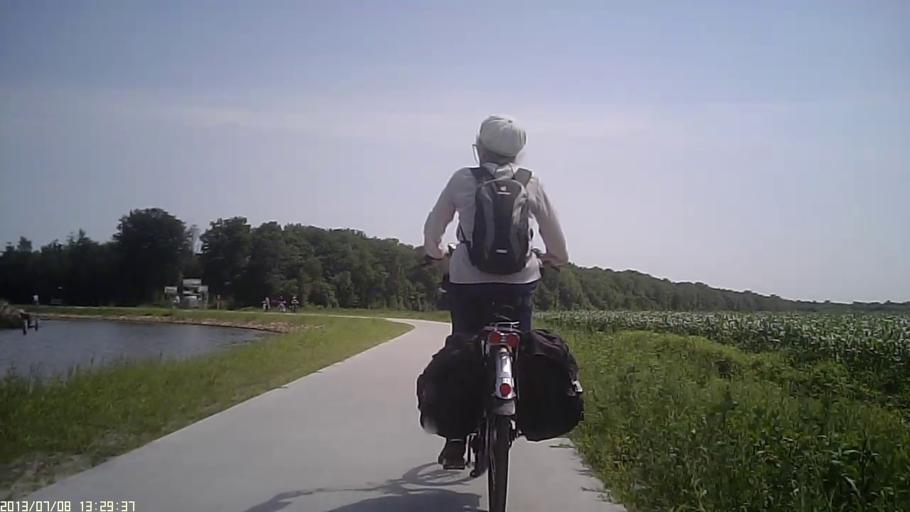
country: NL
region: Drenthe
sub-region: Gemeente Emmen
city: Klazienaveen
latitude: 52.7431
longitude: 6.9865
